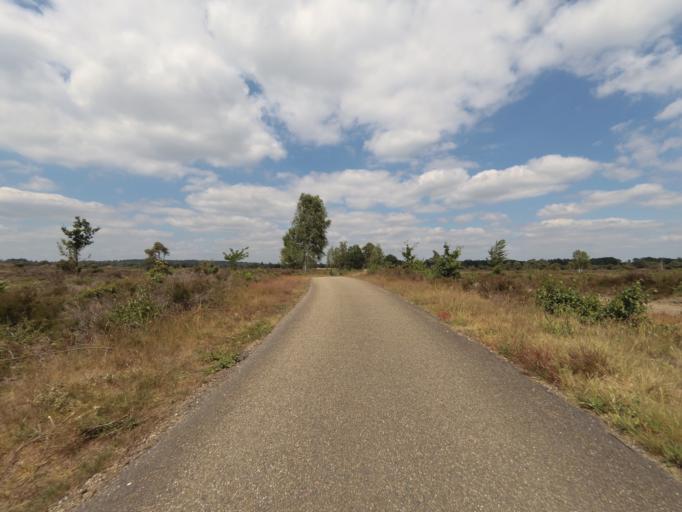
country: NL
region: Overijssel
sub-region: Gemeente Hof van Twente
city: Markelo
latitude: 52.3363
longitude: 6.4511
